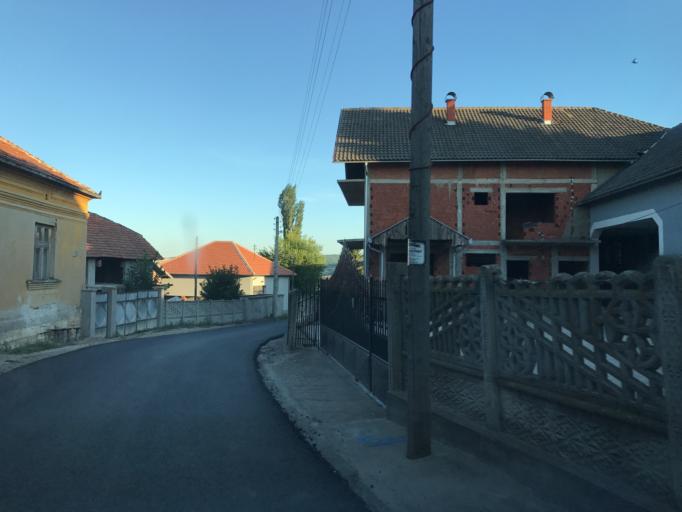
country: BG
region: Vidin
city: Bregovo
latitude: 44.1240
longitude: 22.5986
